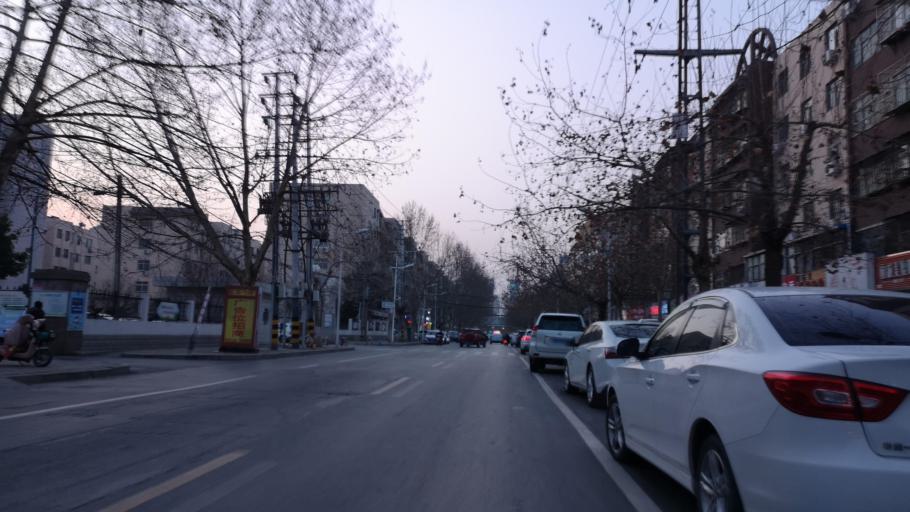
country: CN
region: Henan Sheng
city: Zhongyuanlu
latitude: 35.7659
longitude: 115.0674
